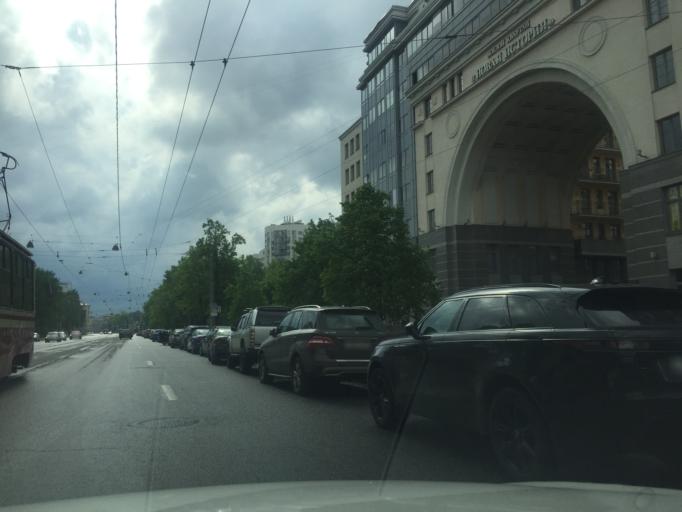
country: RU
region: St.-Petersburg
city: Vasyl'evsky Ostrov
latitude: 59.9364
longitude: 30.2551
